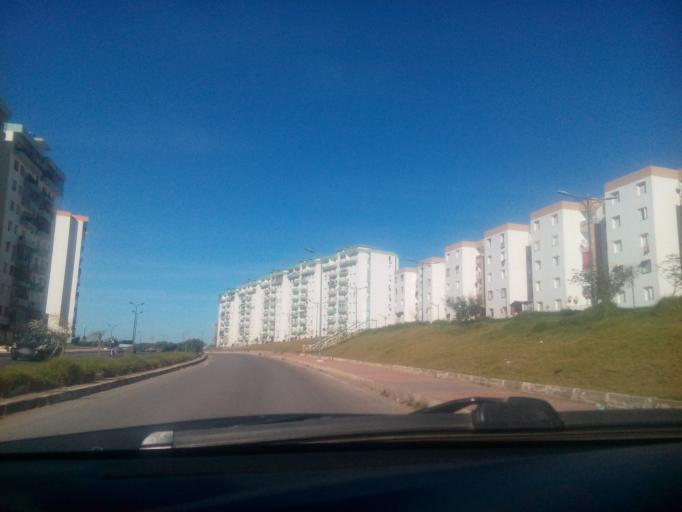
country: DZ
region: Oran
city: Bir el Djir
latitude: 35.7525
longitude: -0.5541
